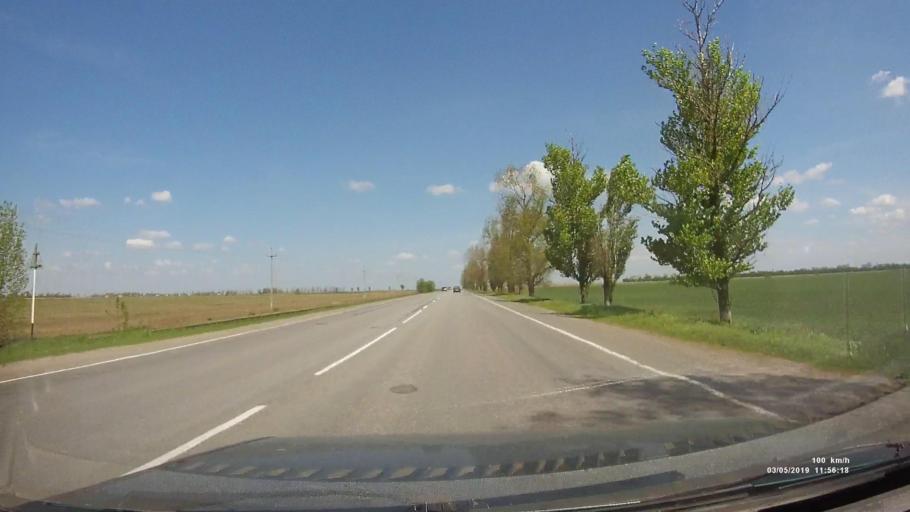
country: RU
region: Rostov
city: Bagayevskaya
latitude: 47.1927
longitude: 40.2996
